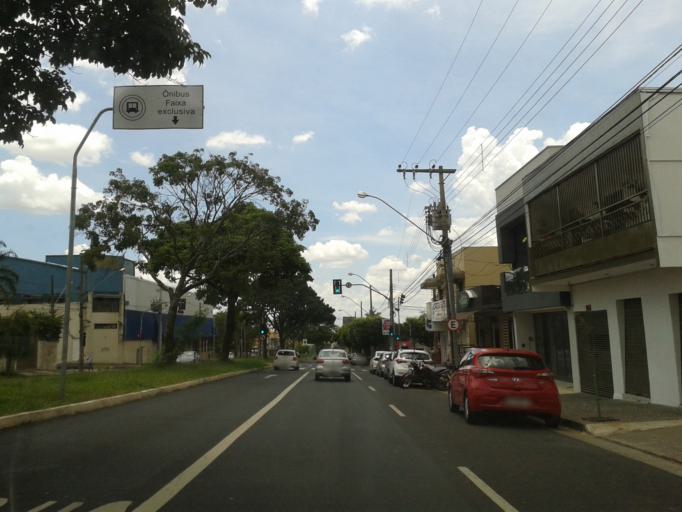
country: BR
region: Minas Gerais
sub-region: Uberlandia
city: Uberlandia
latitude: -18.9184
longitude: -48.2486
